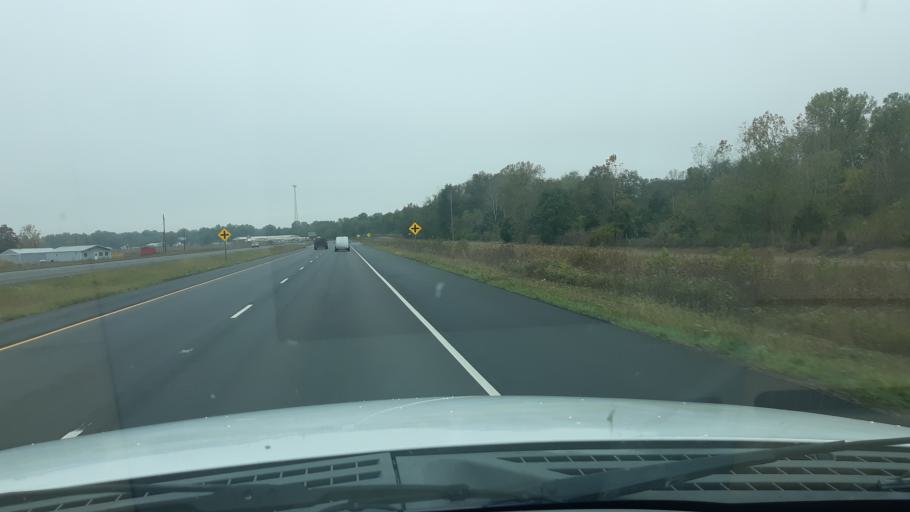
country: US
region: Illinois
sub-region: Saline County
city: Harrisburg
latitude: 37.7734
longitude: -88.5061
